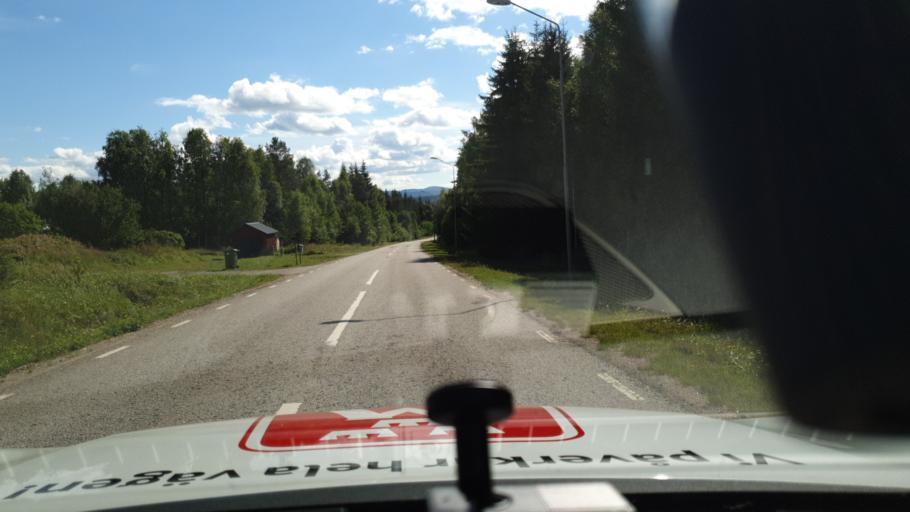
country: NO
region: Hedmark
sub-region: Trysil
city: Innbygda
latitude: 60.9697
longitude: 12.4886
